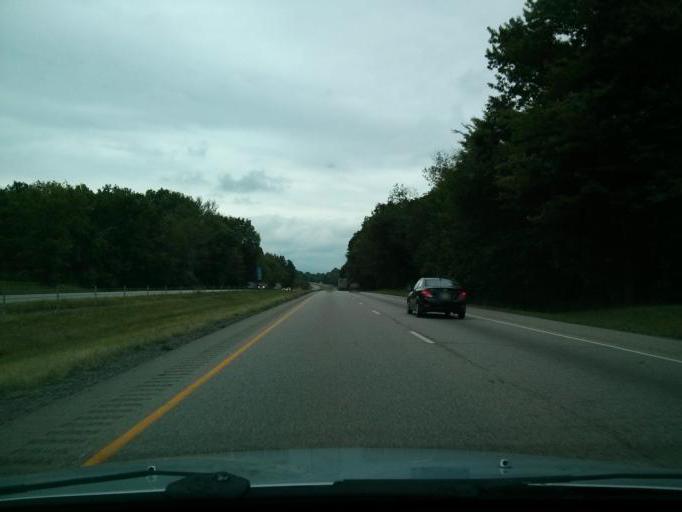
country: US
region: Ohio
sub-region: Portage County
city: Brimfield
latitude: 41.1087
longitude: -81.3099
